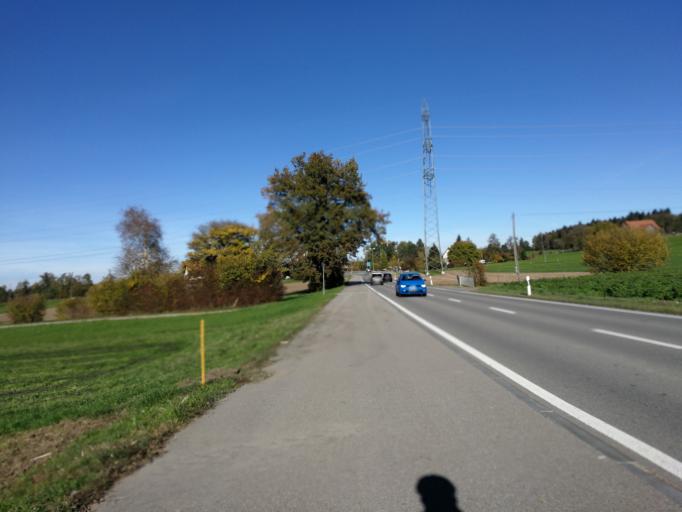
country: CH
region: Zurich
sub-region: Bezirk Meilen
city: Oetwil am See
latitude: 47.2855
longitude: 8.7305
